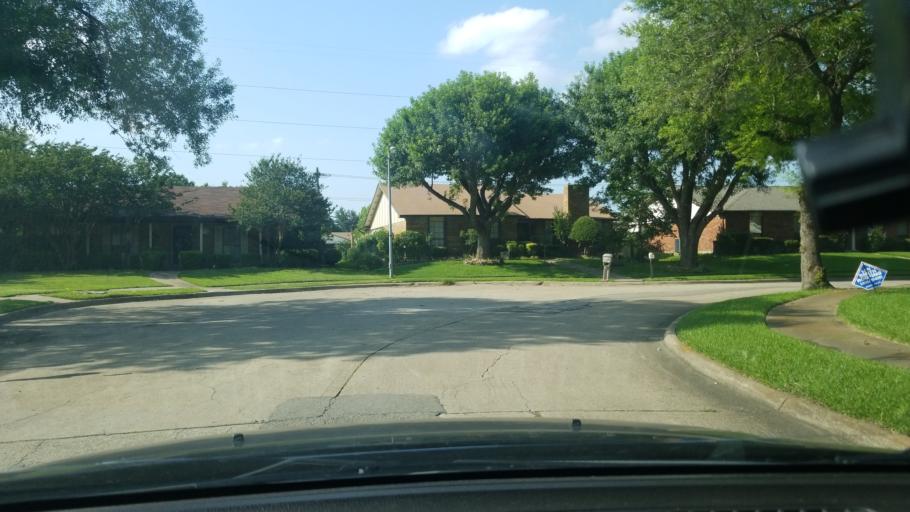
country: US
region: Texas
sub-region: Dallas County
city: Sunnyvale
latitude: 32.8188
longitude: -96.6065
